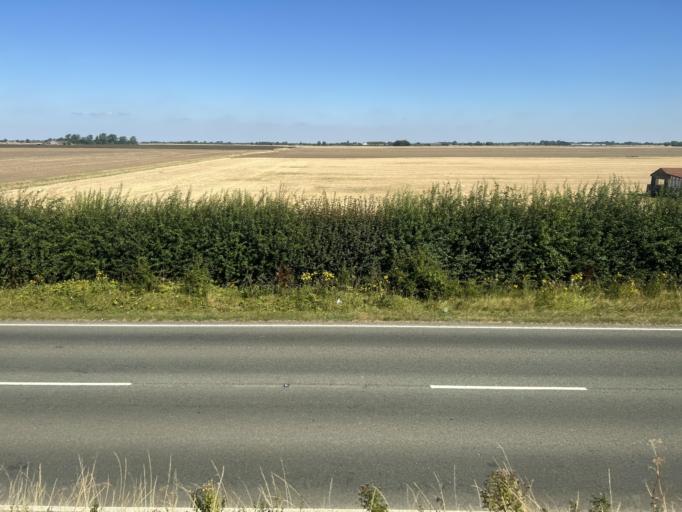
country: GB
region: England
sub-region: Lincolnshire
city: Kirton
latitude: 52.9742
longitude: -0.0909
